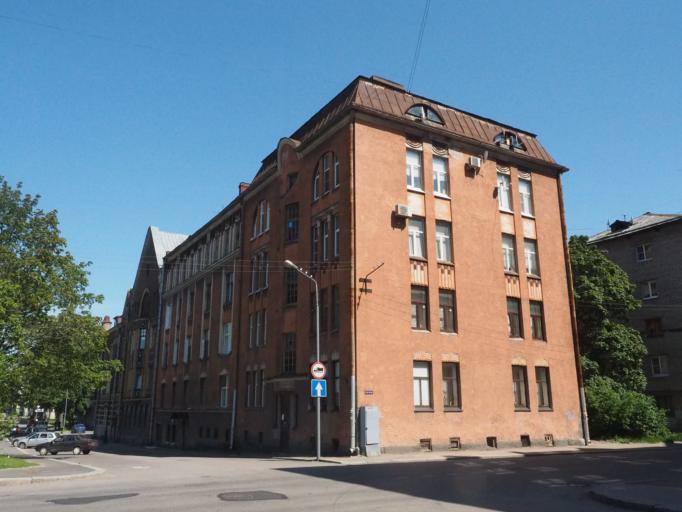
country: RU
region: Leningrad
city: Vyborg
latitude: 60.7054
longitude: 28.7426
